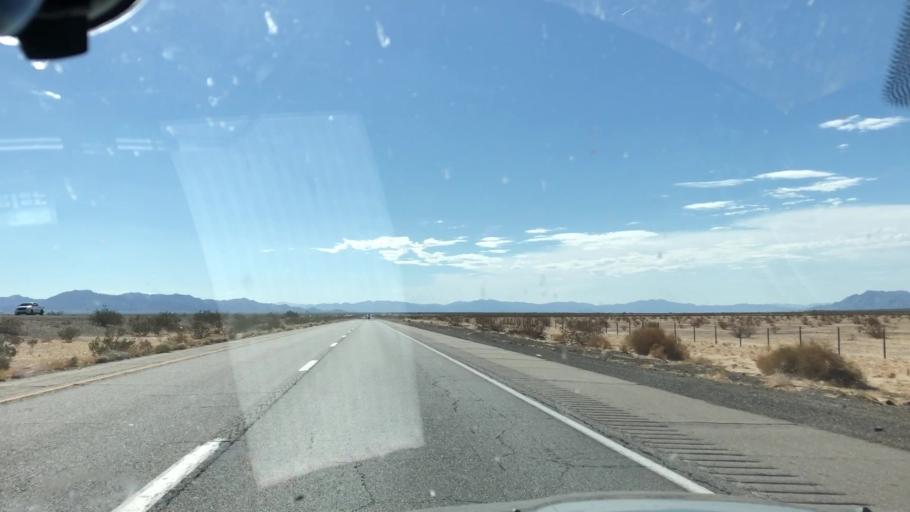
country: US
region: California
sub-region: Riverside County
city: Mesa Verde
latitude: 33.6392
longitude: -115.0937
